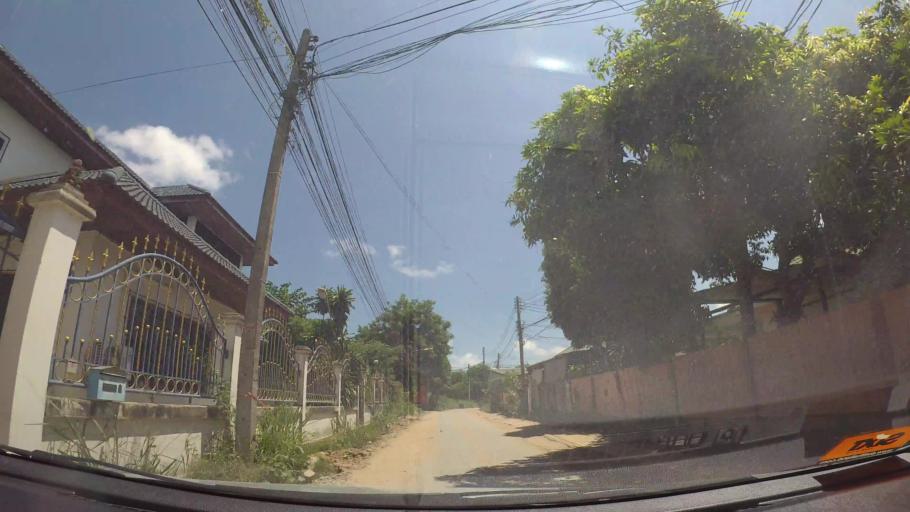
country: TH
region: Rayong
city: Rayong
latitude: 12.6900
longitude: 101.2674
